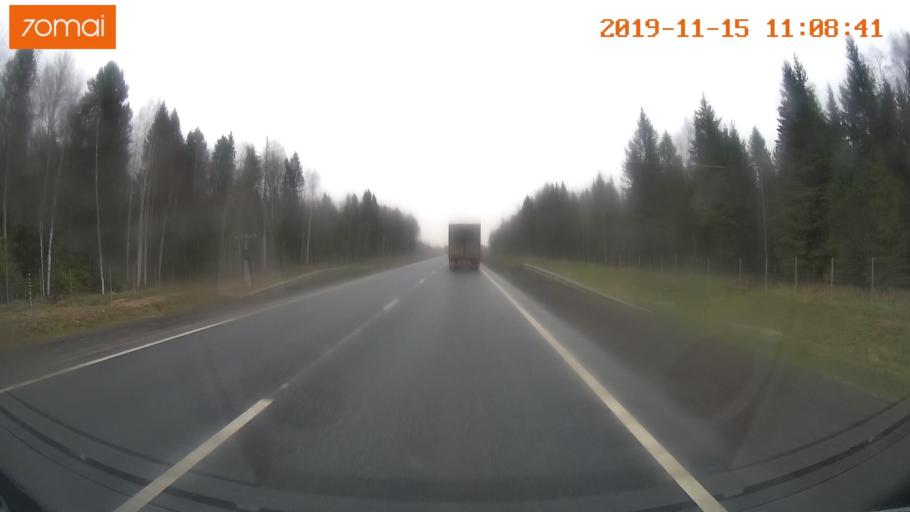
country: RU
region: Vologda
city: Chebsara
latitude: 59.1201
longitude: 39.0793
